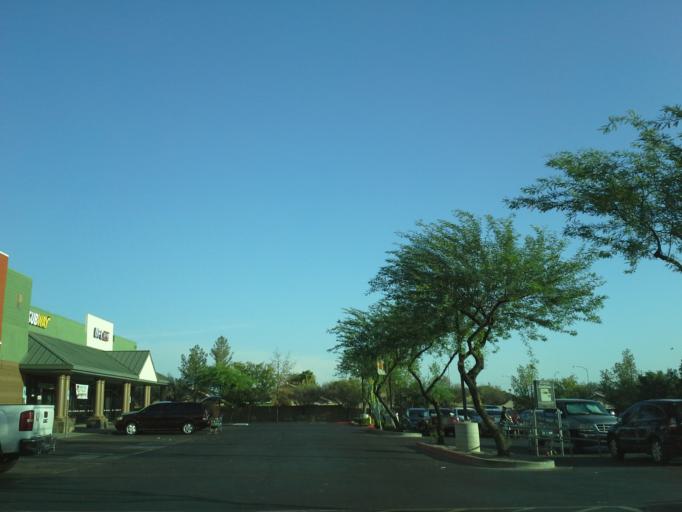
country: US
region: Arizona
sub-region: Pinal County
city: Apache Junction
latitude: 33.4066
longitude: -111.6313
